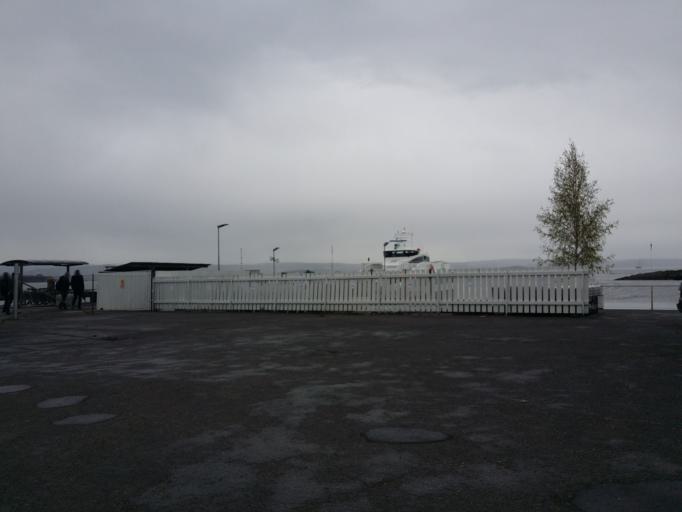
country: NO
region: Akershus
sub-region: Baerum
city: Lysaker
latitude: 59.8940
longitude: 10.6331
